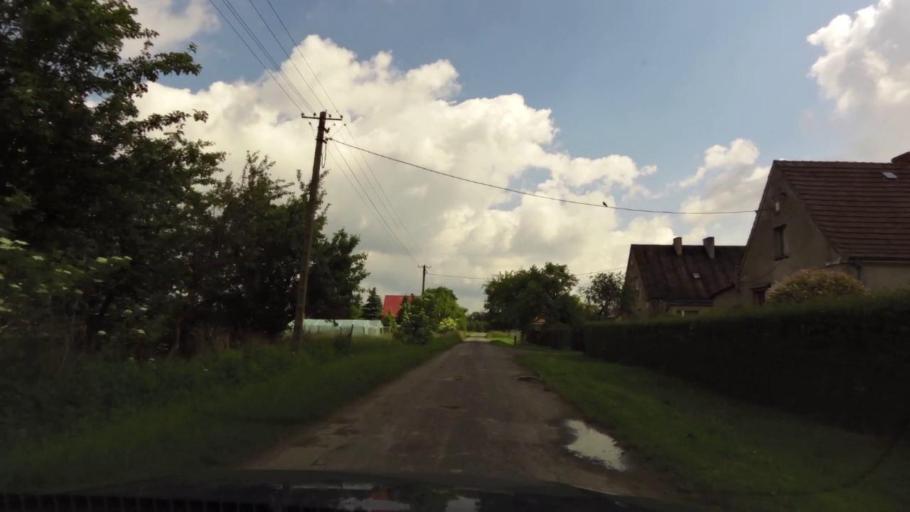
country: PL
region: West Pomeranian Voivodeship
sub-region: Powiat pyrzycki
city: Lipiany
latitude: 52.9599
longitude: 14.9547
